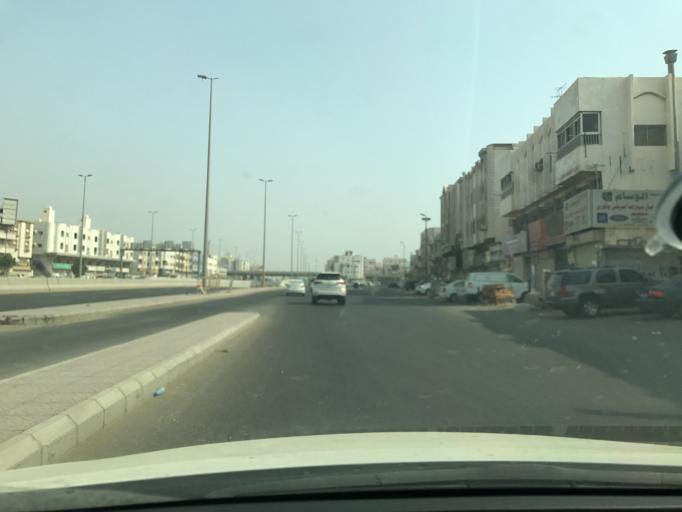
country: SA
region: Makkah
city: Jeddah
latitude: 21.6233
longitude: 39.1845
